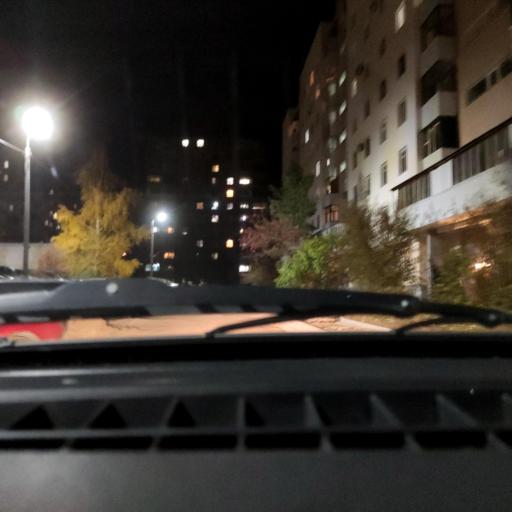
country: RU
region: Bashkortostan
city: Ufa
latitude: 54.8200
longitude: 56.1284
